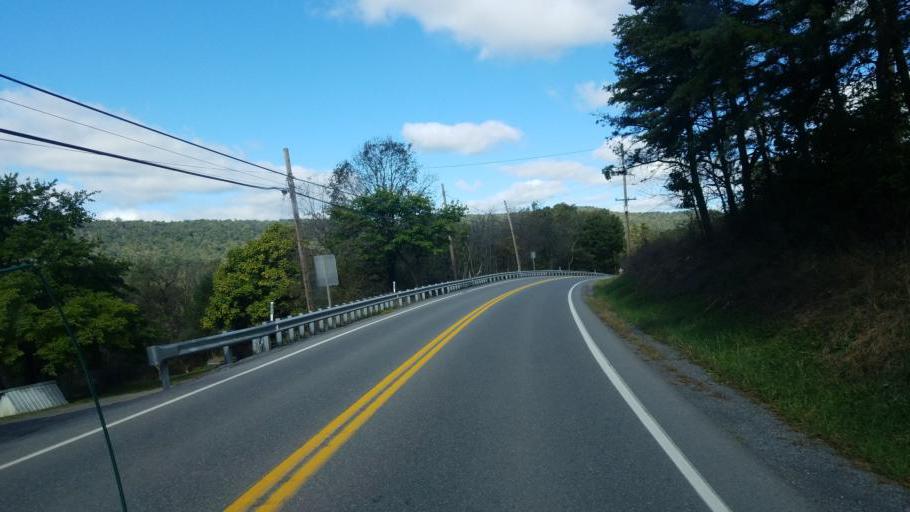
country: US
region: Pennsylvania
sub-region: Fulton County
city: McConnellsburg
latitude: 39.9401
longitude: -78.0195
